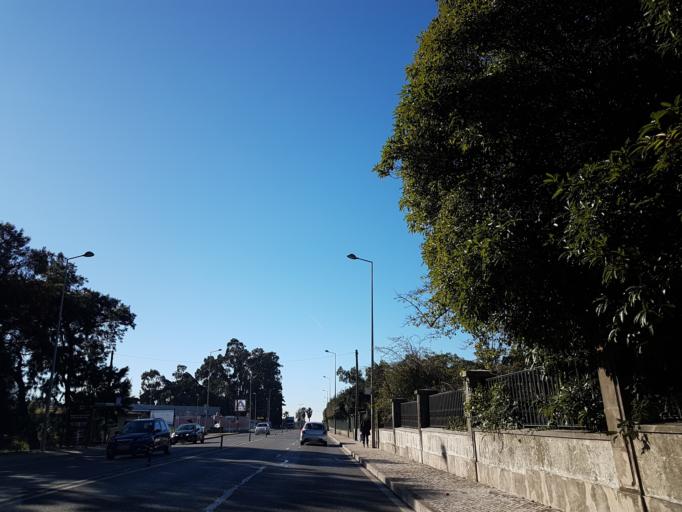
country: PT
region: Lisbon
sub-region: Sintra
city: Sintra
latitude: 38.7756
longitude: -9.3800
